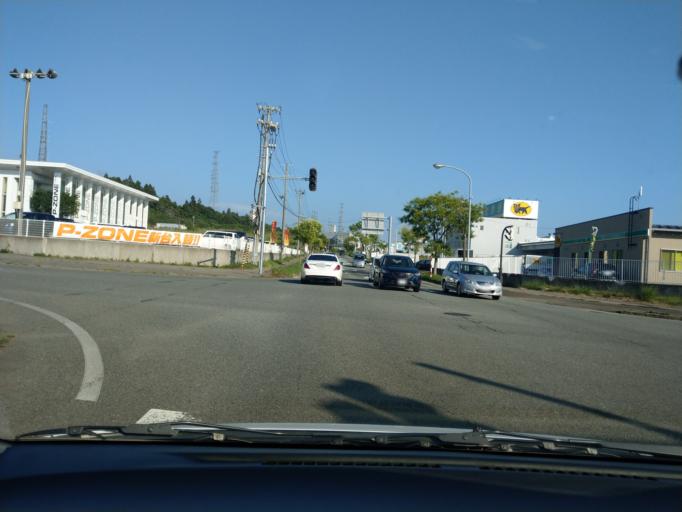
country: JP
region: Akita
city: Akita
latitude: 39.6599
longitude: 140.1705
